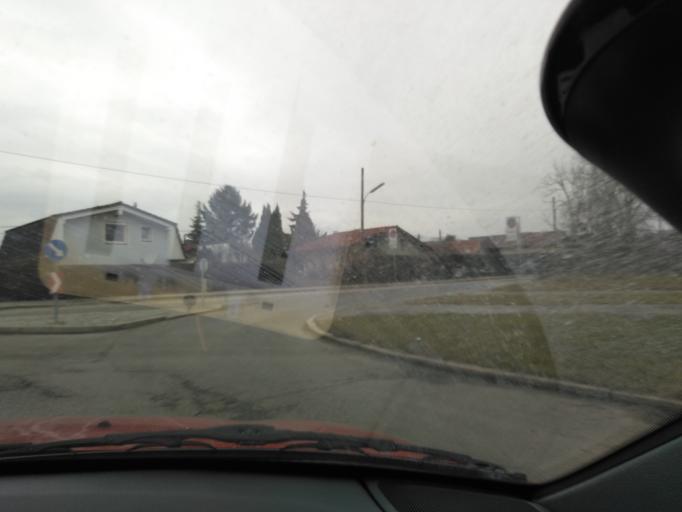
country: AT
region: Lower Austria
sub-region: Politischer Bezirk Modling
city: Vosendorf
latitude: 48.1655
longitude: 16.3340
